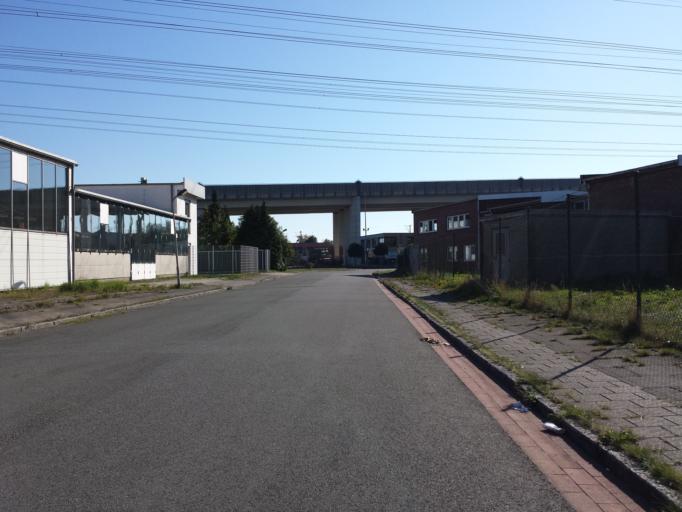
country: DE
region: Lower Saxony
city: Ritterhude
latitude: 53.1439
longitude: 8.7225
